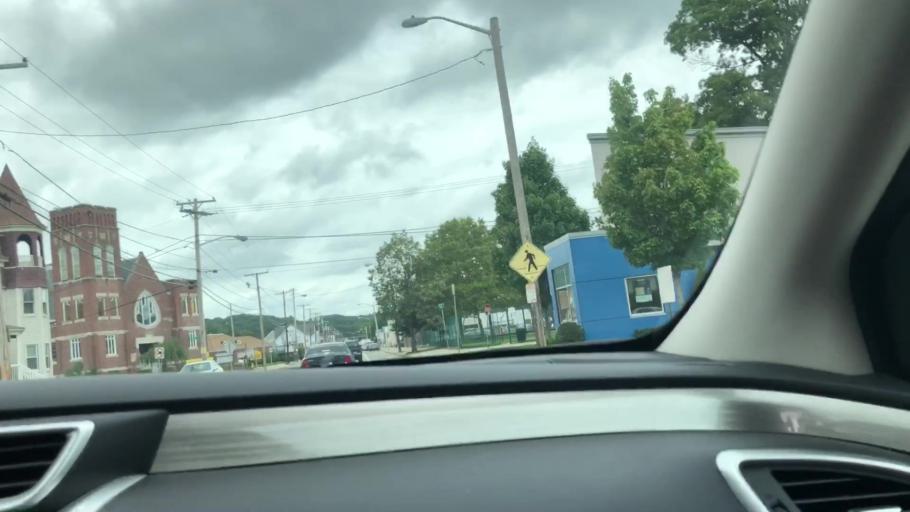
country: US
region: Rhode Island
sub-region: Providence County
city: Central Falls
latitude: 41.8752
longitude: -71.4146
